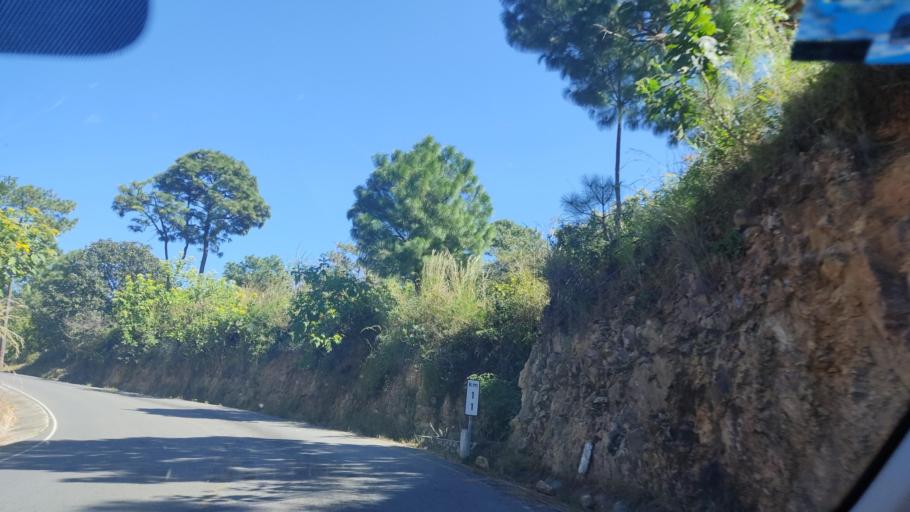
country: MX
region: Nayarit
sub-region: Jala
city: Rosa Blanca
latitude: 21.0948
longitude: -104.3806
